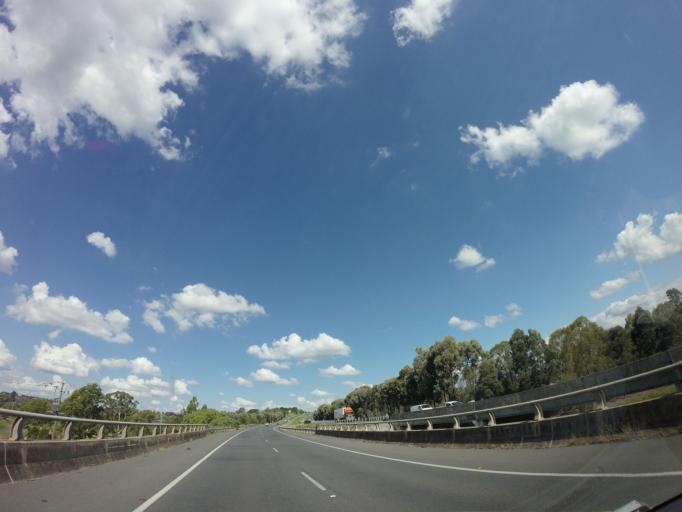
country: AU
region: Queensland
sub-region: Ipswich
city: Thagoona
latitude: -27.5629
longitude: 152.5957
